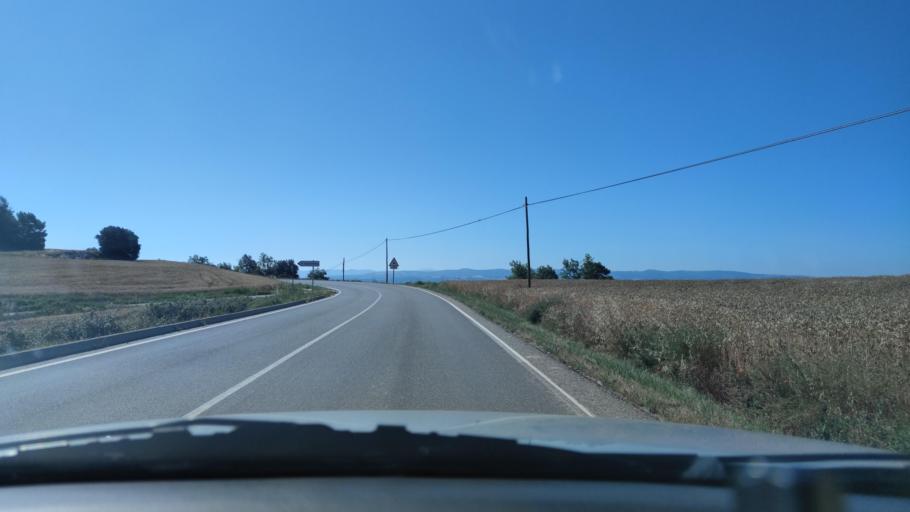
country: ES
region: Catalonia
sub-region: Provincia de Lleida
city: Solsona
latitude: 41.9147
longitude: 1.5063
